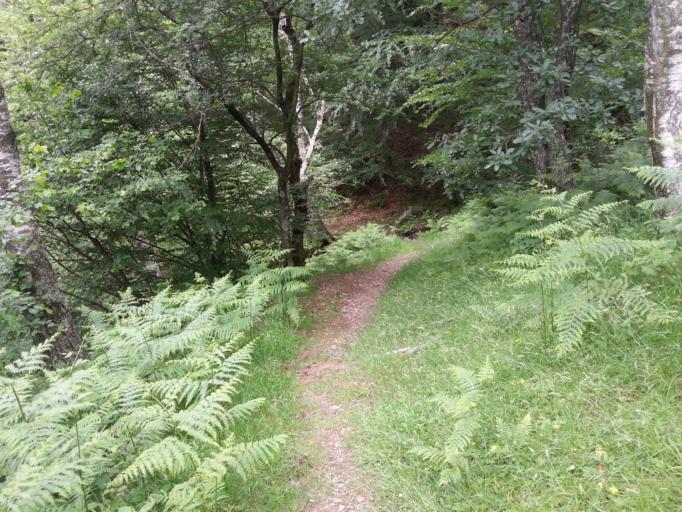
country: CH
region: Ticino
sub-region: Lugano District
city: Tesserete
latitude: 46.1090
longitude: 8.9710
